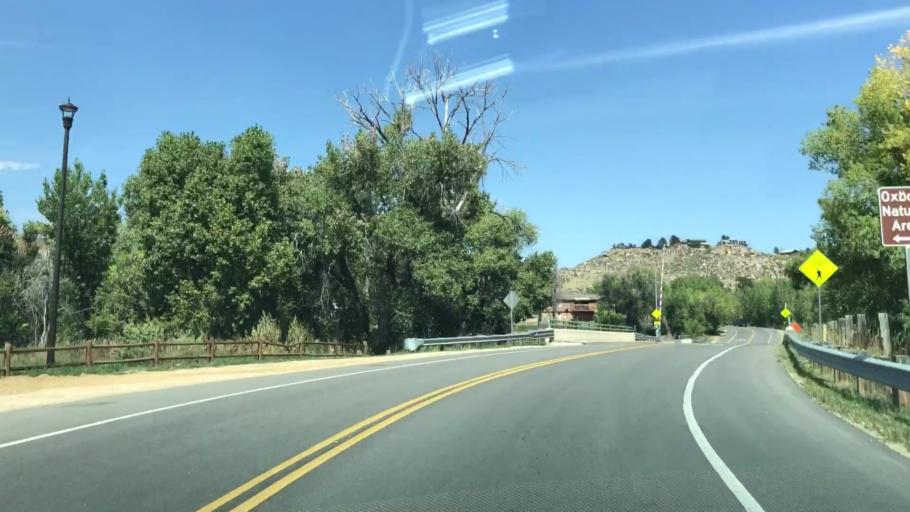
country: US
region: Colorado
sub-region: Larimer County
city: Loveland
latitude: 40.4043
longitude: -105.1416
